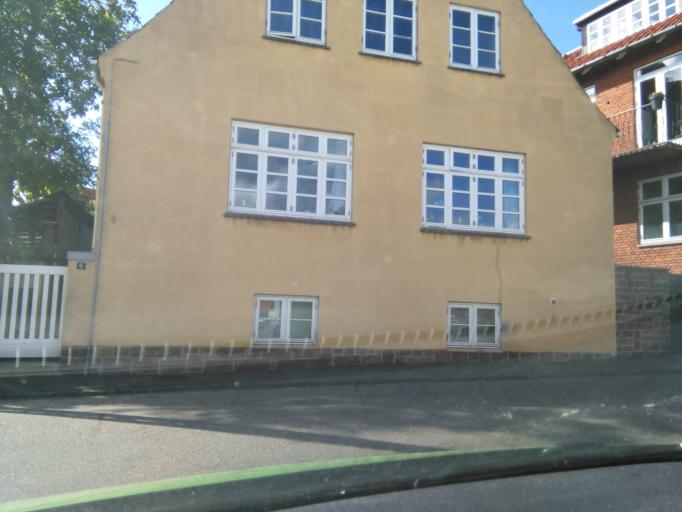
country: DK
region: Capital Region
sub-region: Bornholm Kommune
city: Nexo
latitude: 55.0627
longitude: 15.1300
